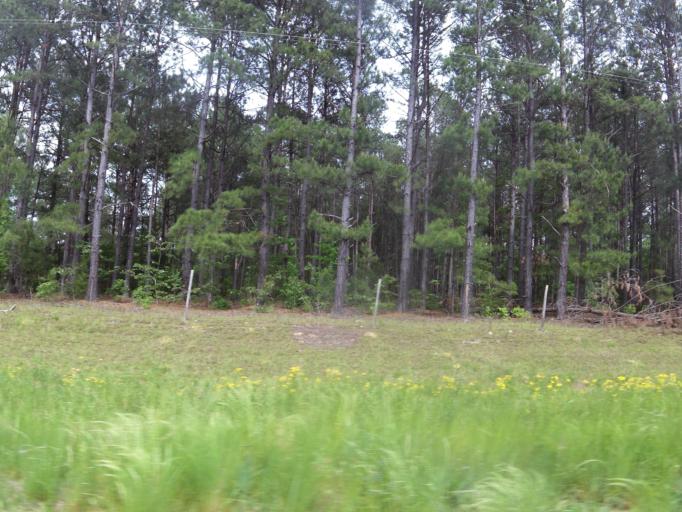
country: US
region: Georgia
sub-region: McDuffie County
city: Thomson
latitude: 33.4227
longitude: -82.4849
